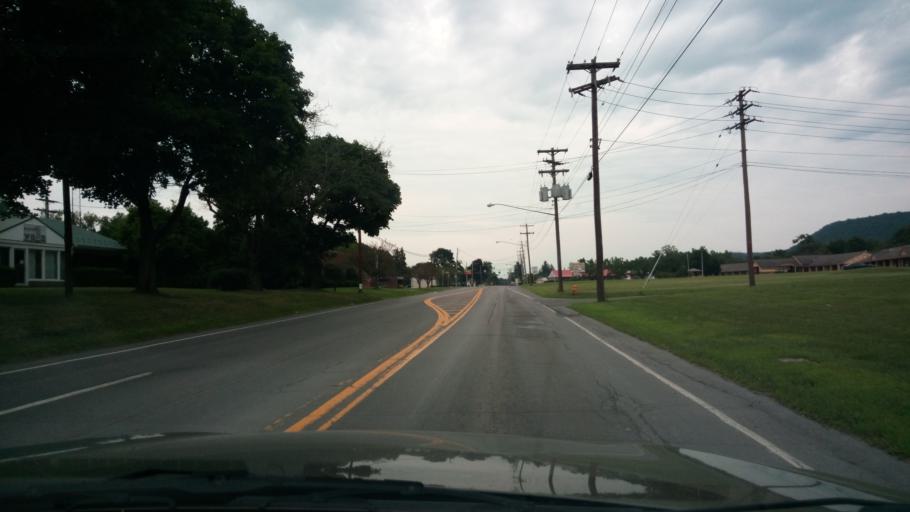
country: US
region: New York
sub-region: Chemung County
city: Elmira Heights
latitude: 42.1203
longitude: -76.8090
